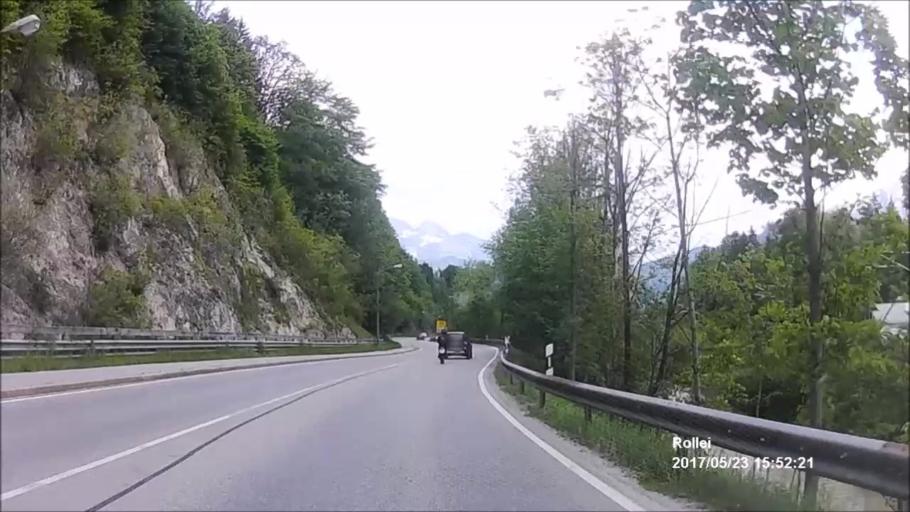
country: DE
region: Bavaria
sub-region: Upper Bavaria
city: Bischofswiesen
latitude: 47.6465
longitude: 12.9697
